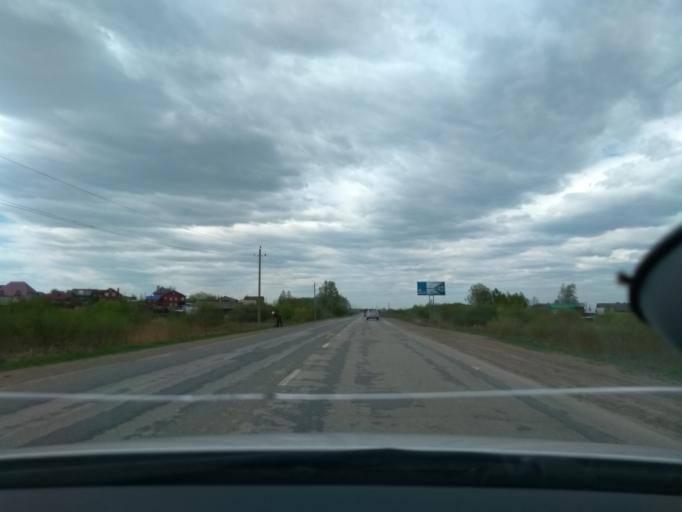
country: RU
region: Perm
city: Lobanovo
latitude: 57.8722
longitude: 56.2812
